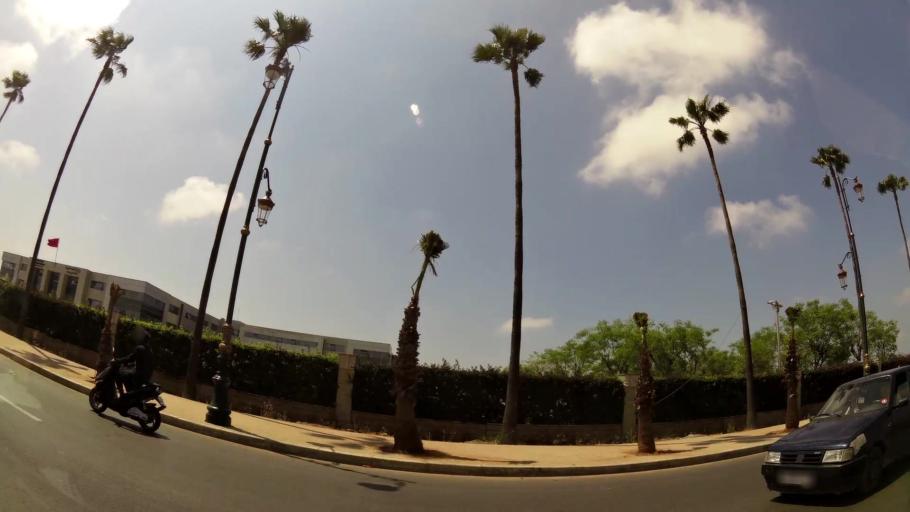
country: MA
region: Rabat-Sale-Zemmour-Zaer
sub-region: Skhirate-Temara
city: Temara
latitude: 33.9659
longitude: -6.8707
